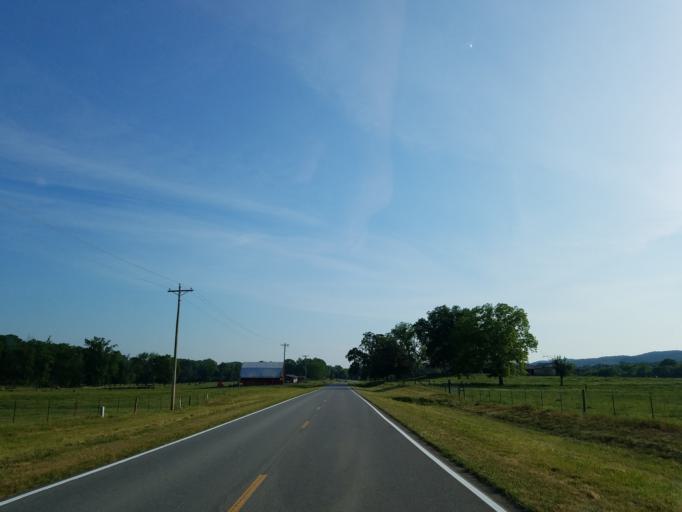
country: US
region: Georgia
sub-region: Chattooga County
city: Trion
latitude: 34.5016
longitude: -85.2438
